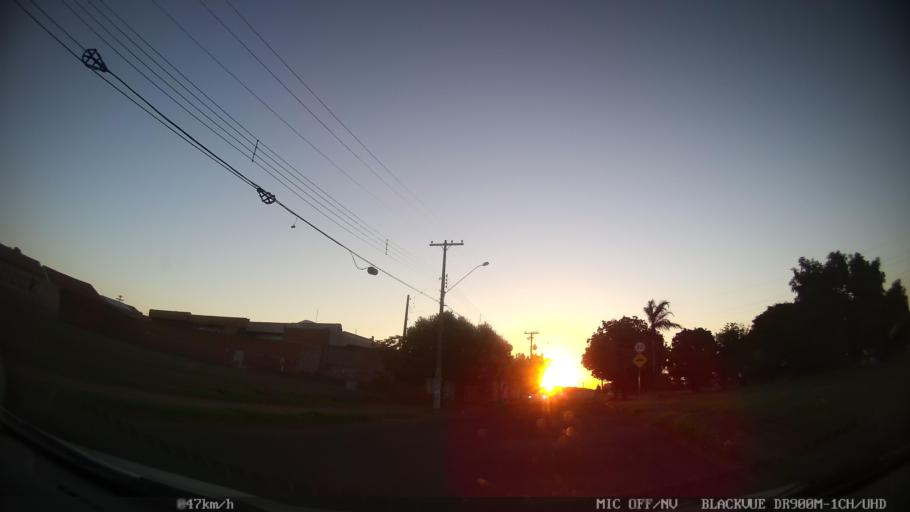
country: BR
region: Sao Paulo
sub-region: Sao Jose Do Rio Preto
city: Sao Jose do Rio Preto
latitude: -20.7964
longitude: -49.3458
